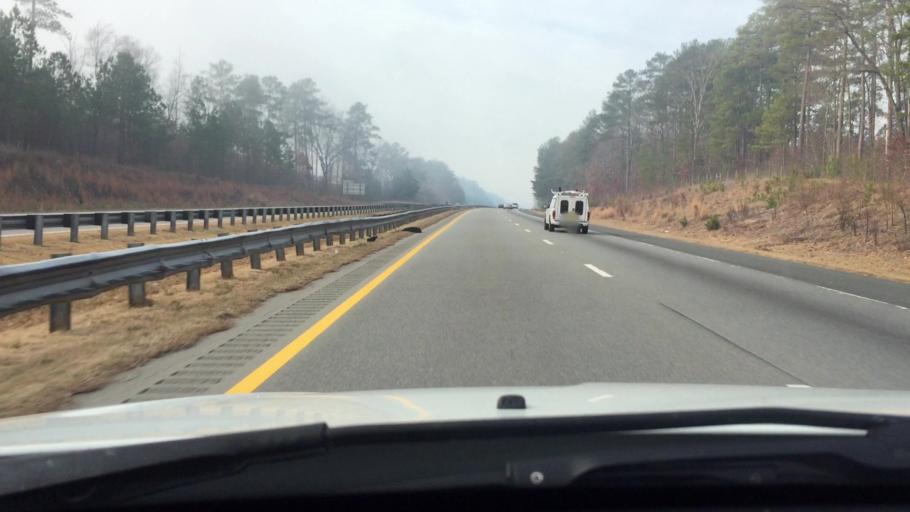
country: US
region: North Carolina
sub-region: Wake County
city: Holly Springs
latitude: 35.6533
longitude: -78.9610
